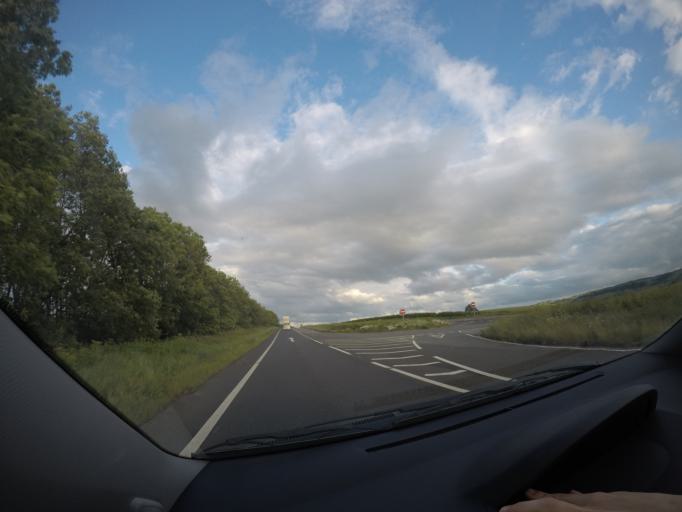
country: GB
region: England
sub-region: County Durham
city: Hutton Magna
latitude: 54.4905
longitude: -1.8094
